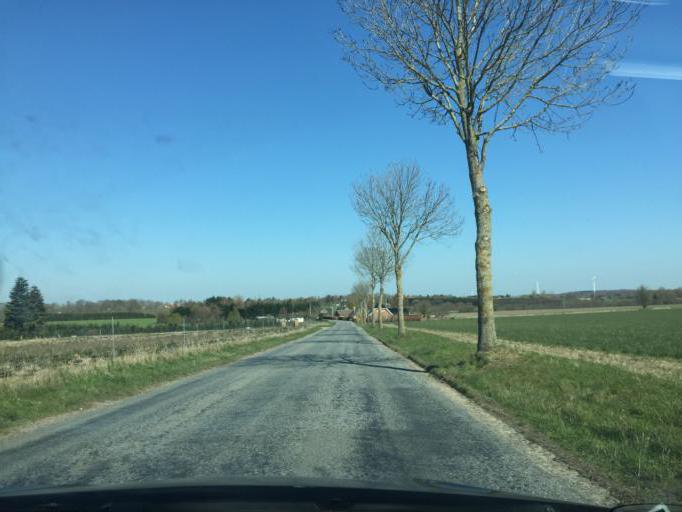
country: DK
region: South Denmark
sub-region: Faaborg-Midtfyn Kommune
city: Ringe
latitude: 55.2754
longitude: 10.5359
